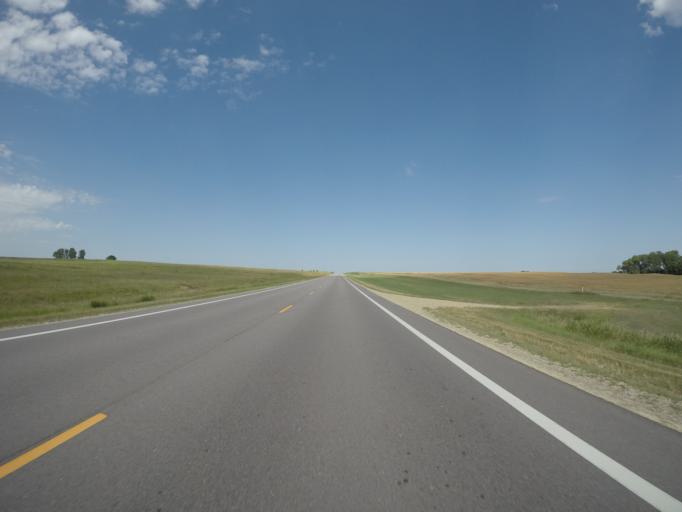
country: US
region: Kansas
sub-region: Clay County
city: Clay Center
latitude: 39.3788
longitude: -97.3150
